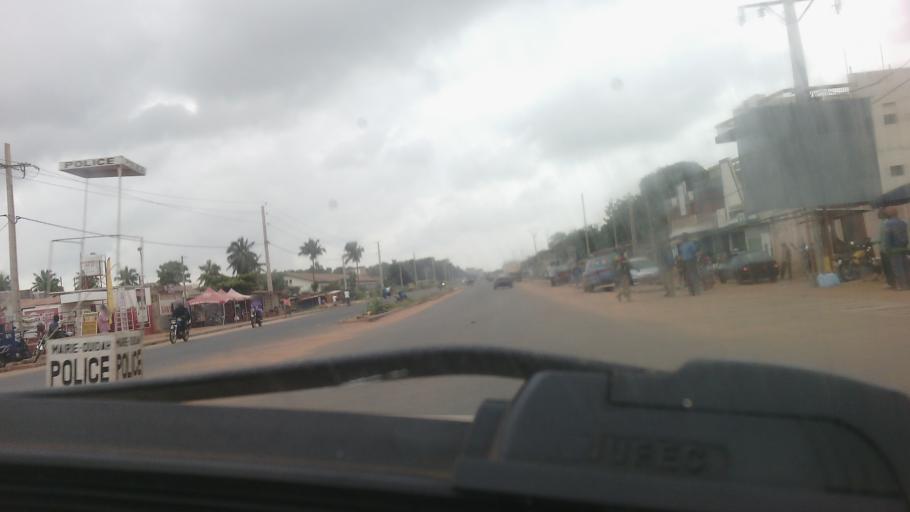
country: BJ
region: Atlantique
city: Ouidah
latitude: 6.3719
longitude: 2.0745
